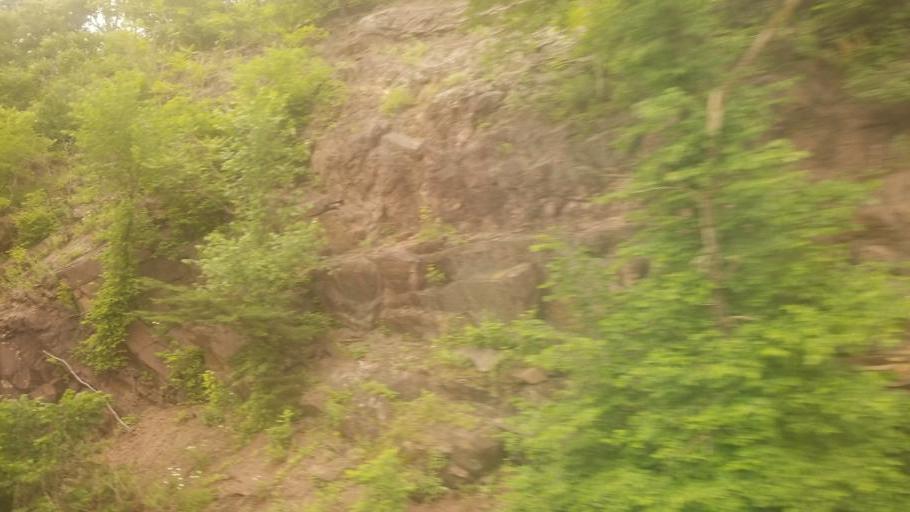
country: US
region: West Virginia
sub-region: Morgan County
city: Berkeley Springs
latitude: 39.6110
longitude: -78.3711
